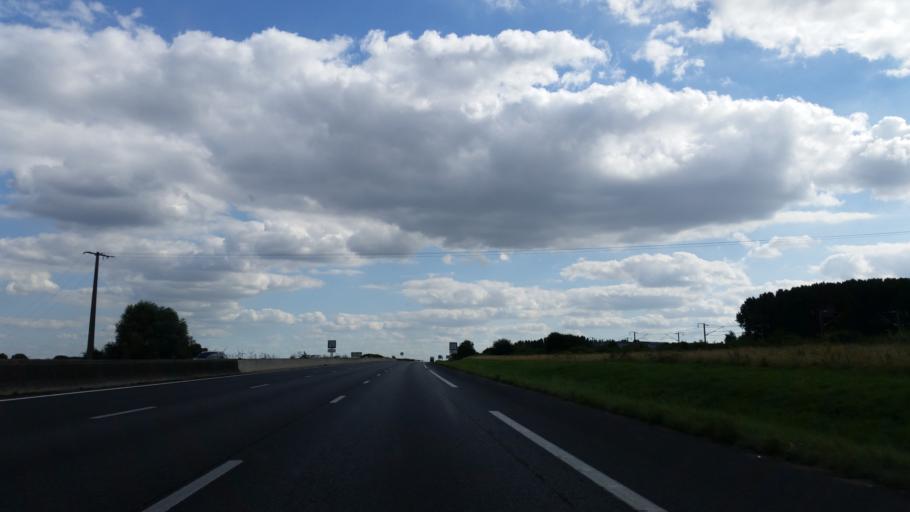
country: FR
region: Nord-Pas-de-Calais
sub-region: Departement du Pas-de-Calais
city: Bapaume
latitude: 50.0951
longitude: 2.8714
